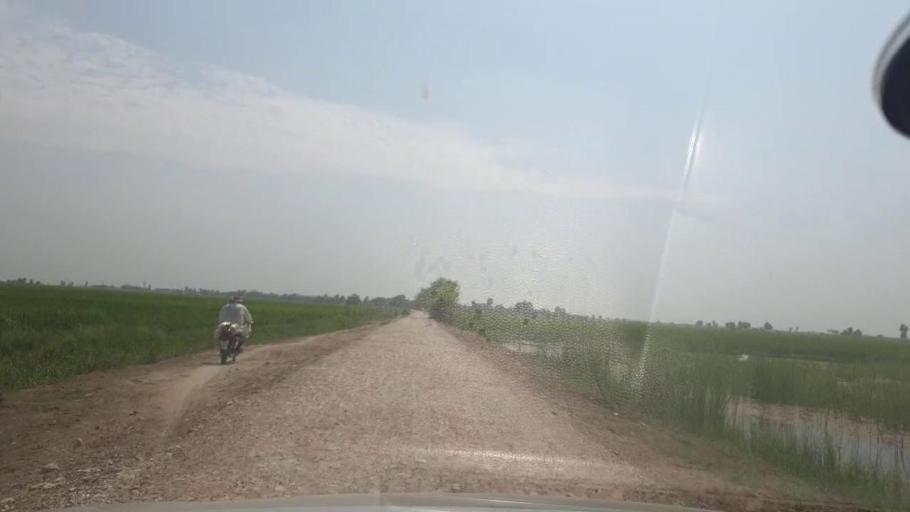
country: PK
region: Sindh
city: Thul
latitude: 28.1658
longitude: 68.6500
